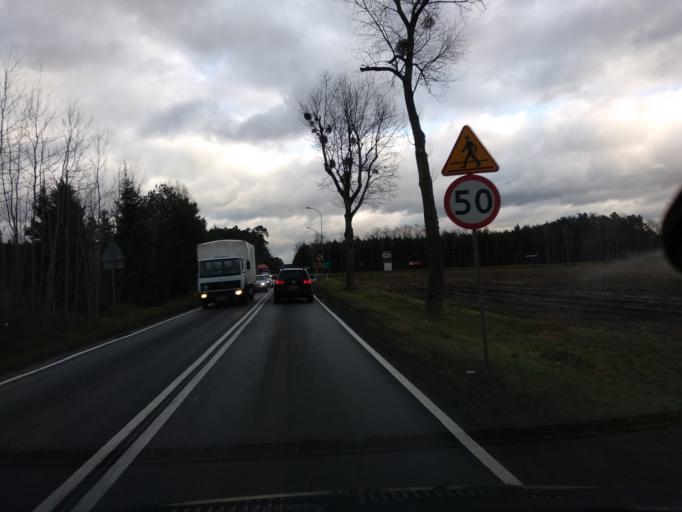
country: PL
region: Greater Poland Voivodeship
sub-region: Powiat ostrowski
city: Jankow Przygodzki
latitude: 51.4942
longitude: 17.7819
